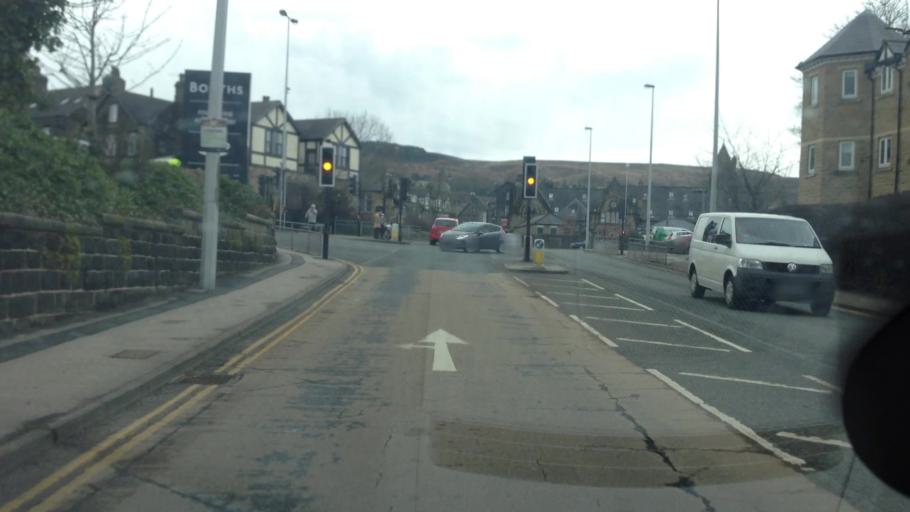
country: GB
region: England
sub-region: Bradford
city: Ilkley
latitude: 53.9279
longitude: -1.8189
